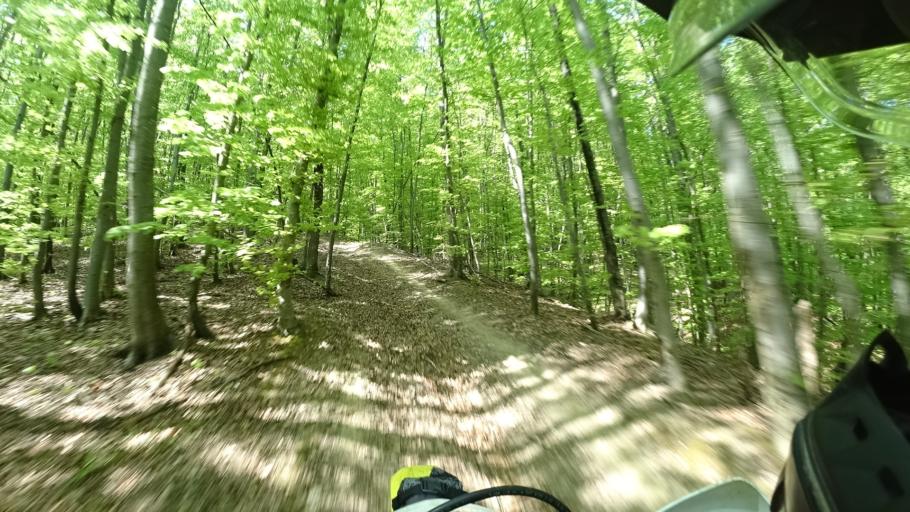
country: HR
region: Grad Zagreb
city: Stenjevec
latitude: 45.8575
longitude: 15.9102
